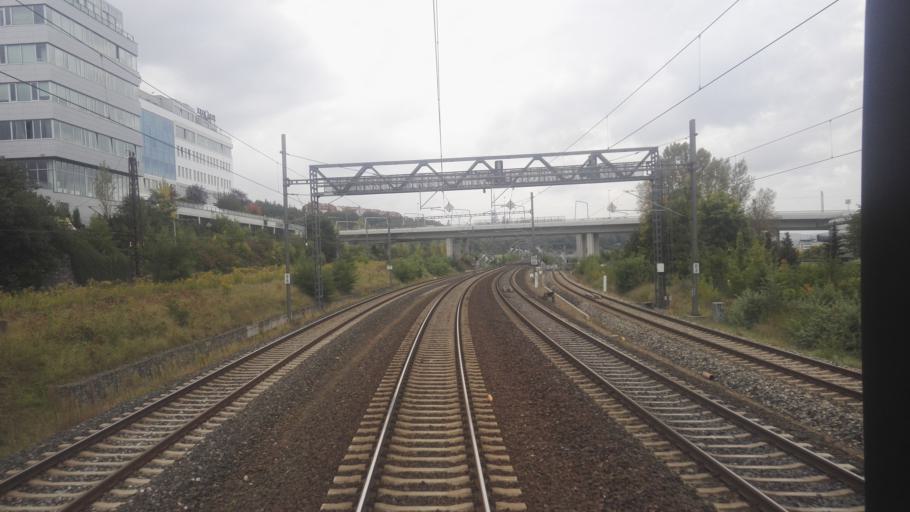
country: CZ
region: Praha
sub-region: Praha 8
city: Liben
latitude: 50.0979
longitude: 14.4776
